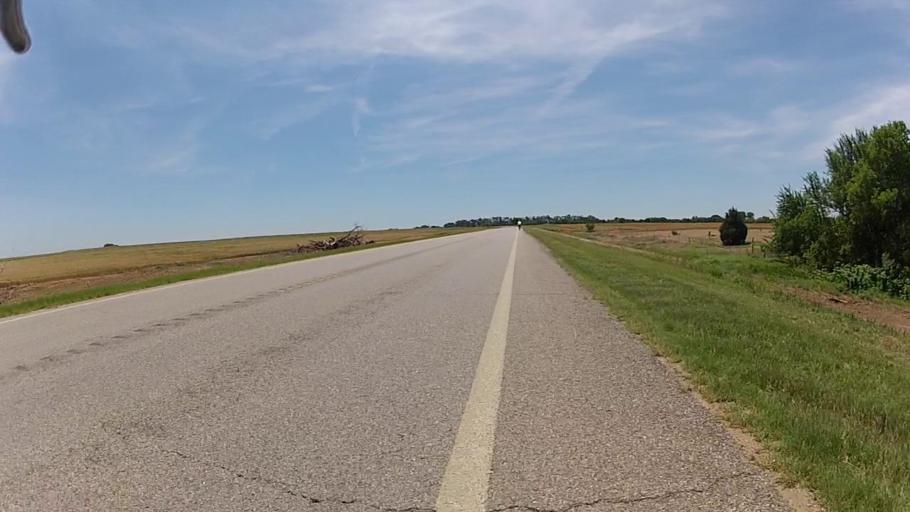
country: US
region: Kansas
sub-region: Barber County
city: Medicine Lodge
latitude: 37.2600
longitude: -98.5274
